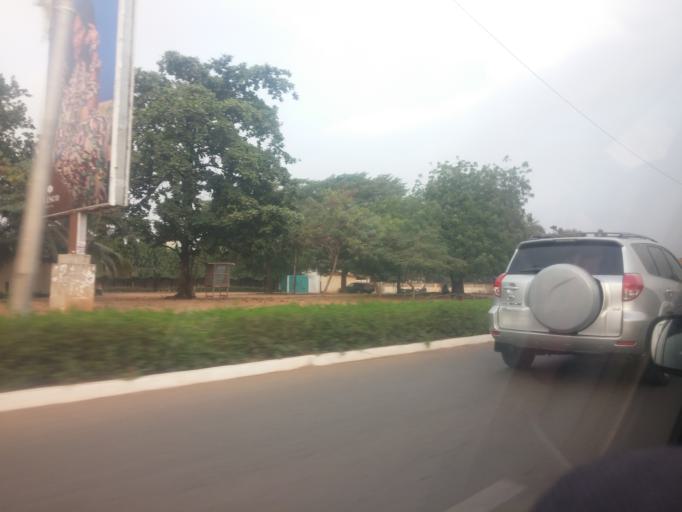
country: TG
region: Maritime
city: Lome
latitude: 6.1621
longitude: 1.2240
